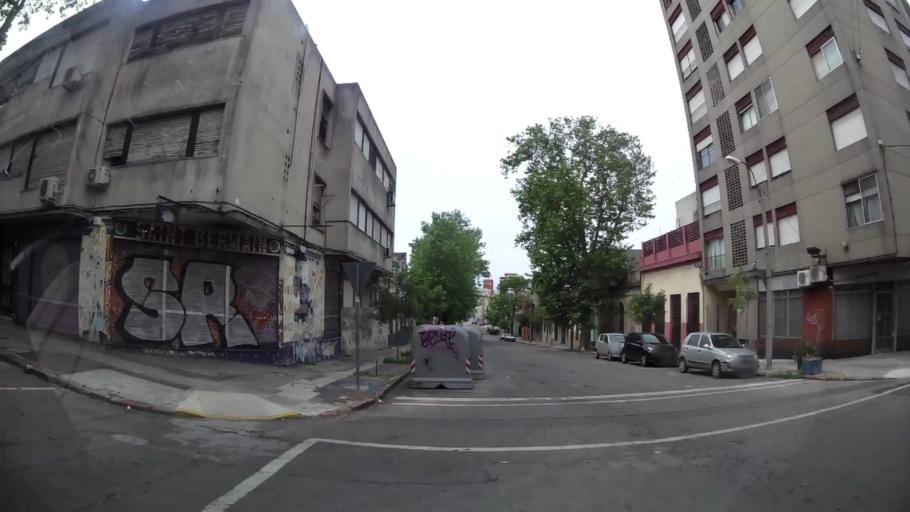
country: UY
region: Montevideo
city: Montevideo
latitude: -34.9104
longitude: -56.1886
